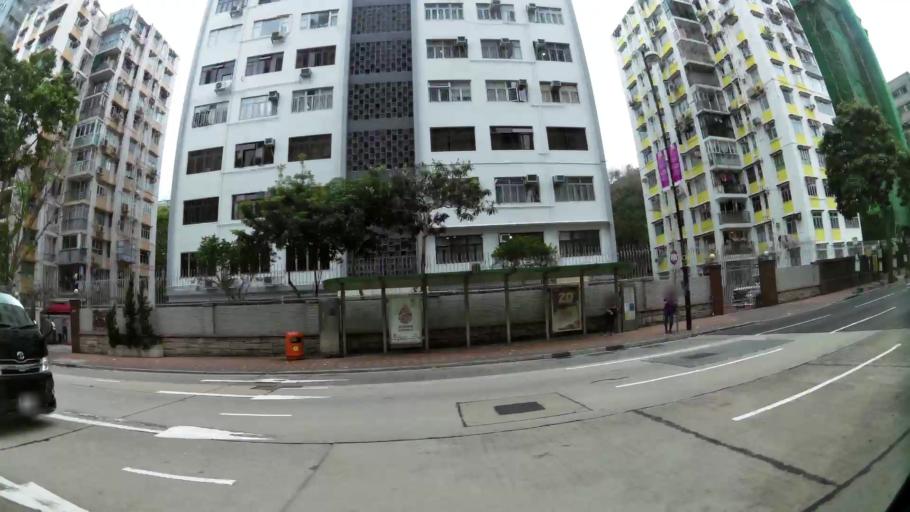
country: HK
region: Kowloon City
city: Kowloon
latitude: 22.3265
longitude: 114.1827
